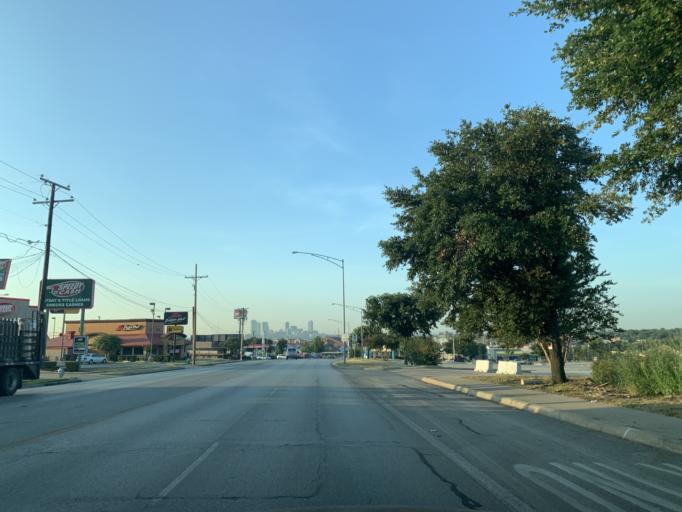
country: US
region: Texas
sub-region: Tarrant County
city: River Oaks
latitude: 32.7969
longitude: -97.3497
